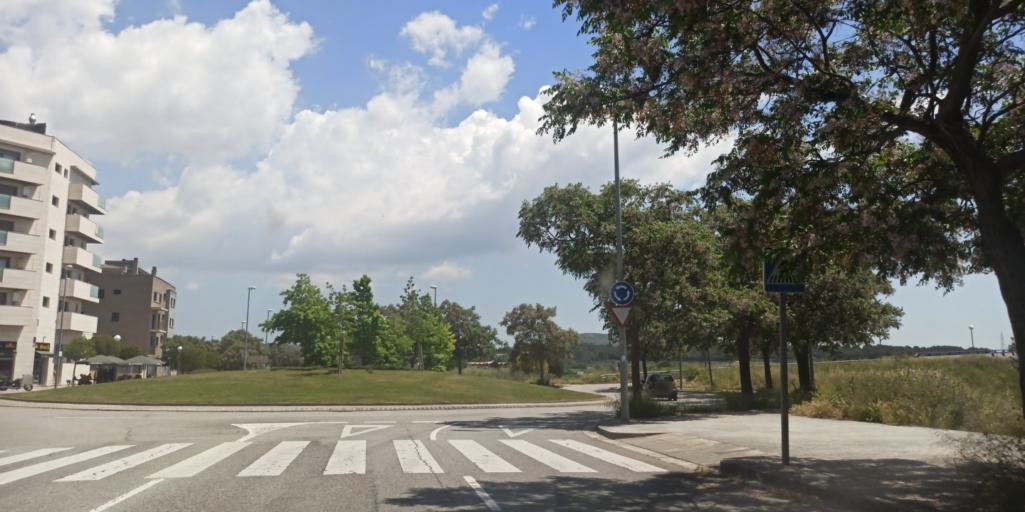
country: ES
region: Catalonia
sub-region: Provincia de Barcelona
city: Vilafranca del Penedes
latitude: 41.3351
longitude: 1.7013
